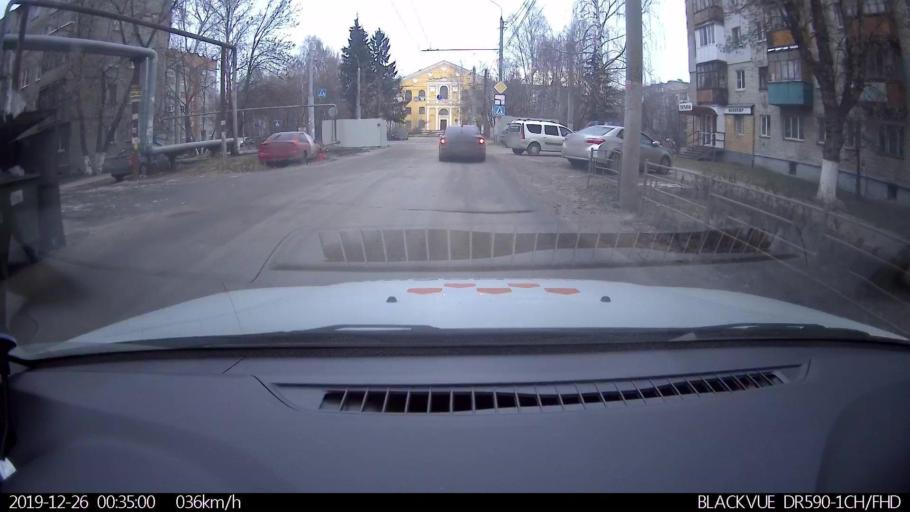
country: RU
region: Nizjnij Novgorod
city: Nizhniy Novgorod
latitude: 56.2915
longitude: 43.9166
